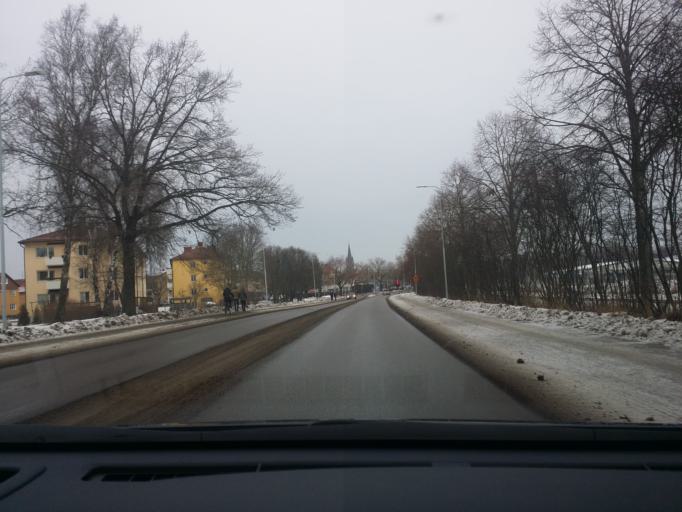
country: SE
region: Vaestra Goetaland
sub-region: Mariestads Kommun
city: Mariestad
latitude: 58.7027
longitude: 13.8203
